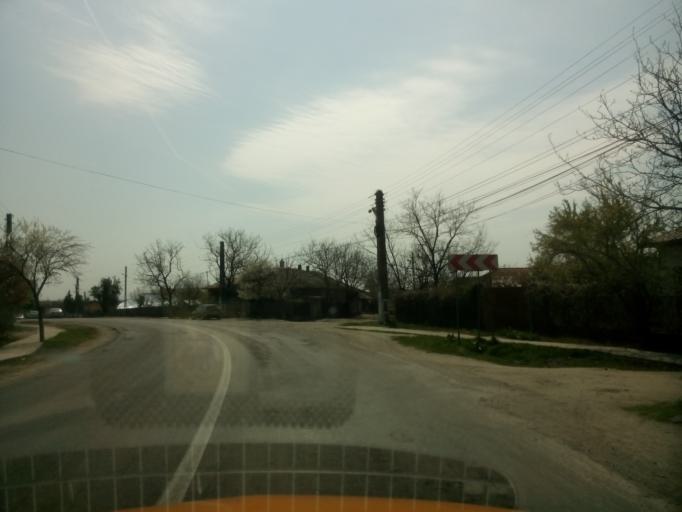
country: RO
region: Calarasi
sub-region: Comuna Soldanu
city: Negoesti
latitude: 44.2298
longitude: 26.5049
